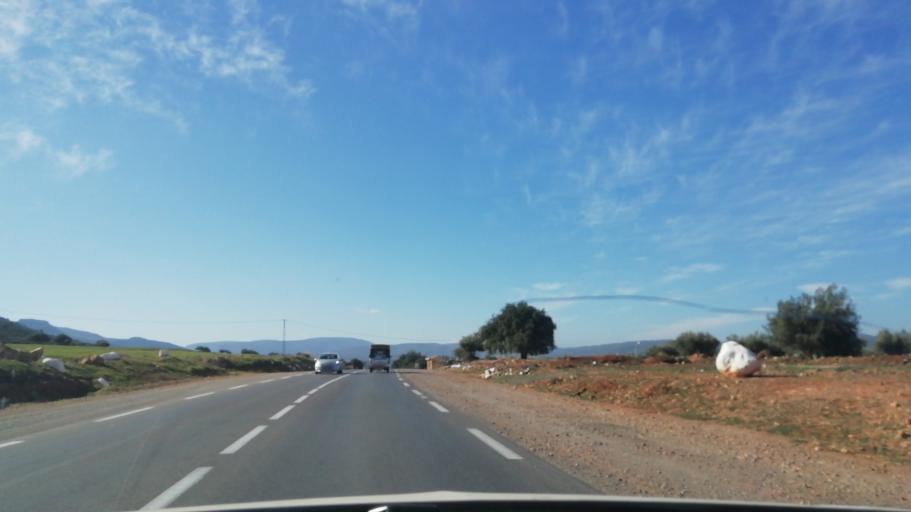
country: DZ
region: Tlemcen
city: Ouled Mimoun
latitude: 34.8859
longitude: -1.0788
